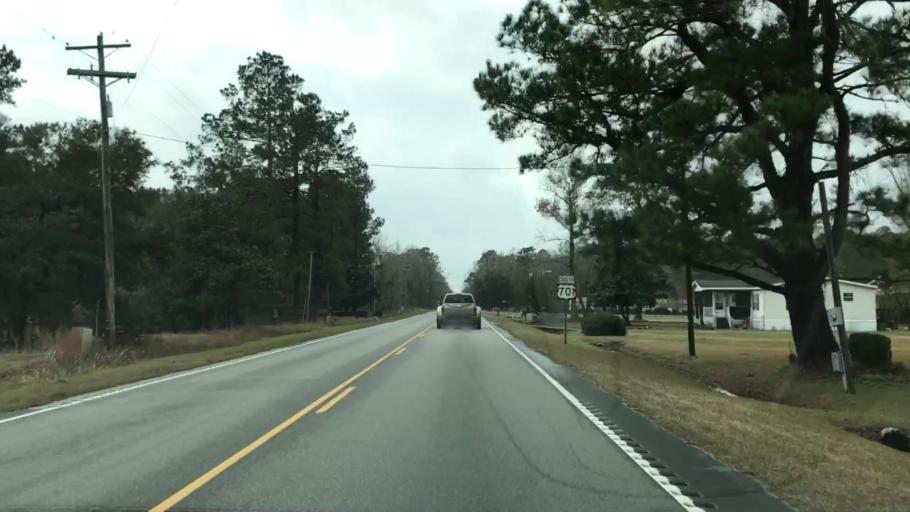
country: US
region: South Carolina
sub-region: Horry County
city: Socastee
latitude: 33.6904
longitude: -79.1182
